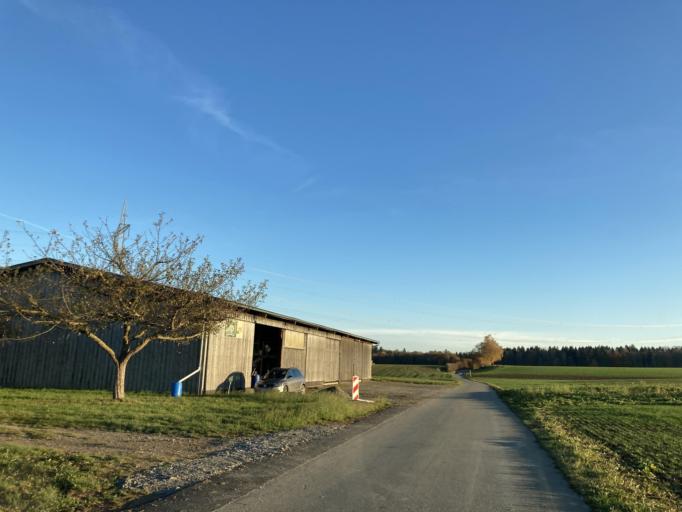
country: DE
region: Baden-Wuerttemberg
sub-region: Tuebingen Region
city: Hirrlingen
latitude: 48.4462
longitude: 8.8845
